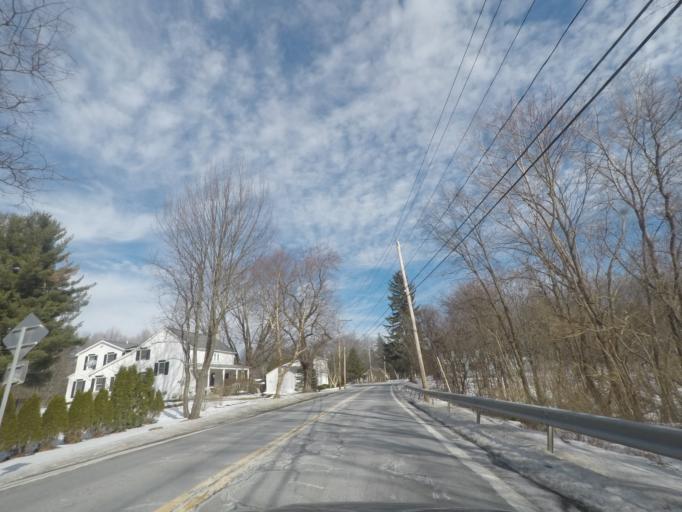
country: US
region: New York
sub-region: Albany County
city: Voorheesville
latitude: 42.6532
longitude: -73.9517
